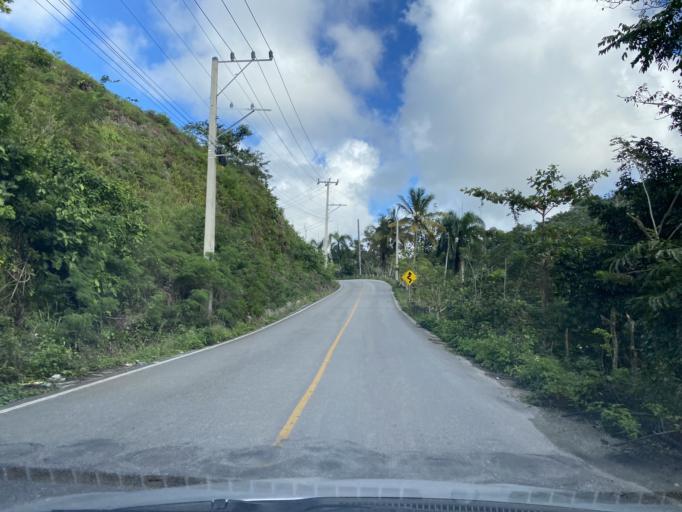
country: DO
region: Samana
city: Las Terrenas
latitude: 19.2680
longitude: -69.5614
